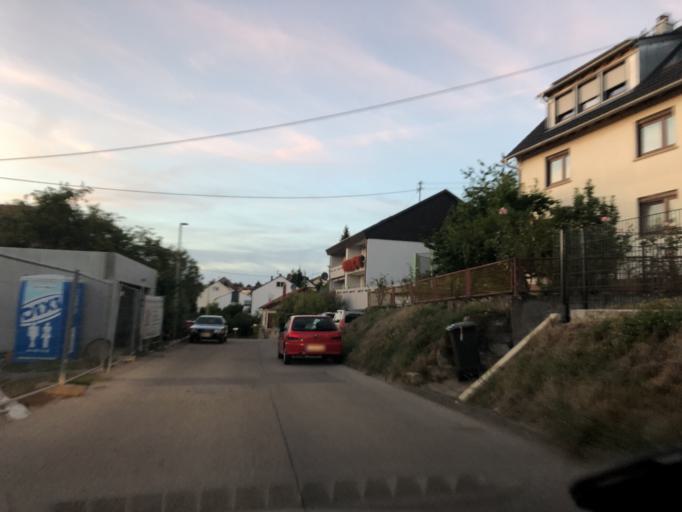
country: DE
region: Baden-Wuerttemberg
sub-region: Regierungsbezirk Stuttgart
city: Erdmannhausen
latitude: 48.8847
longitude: 9.2821
